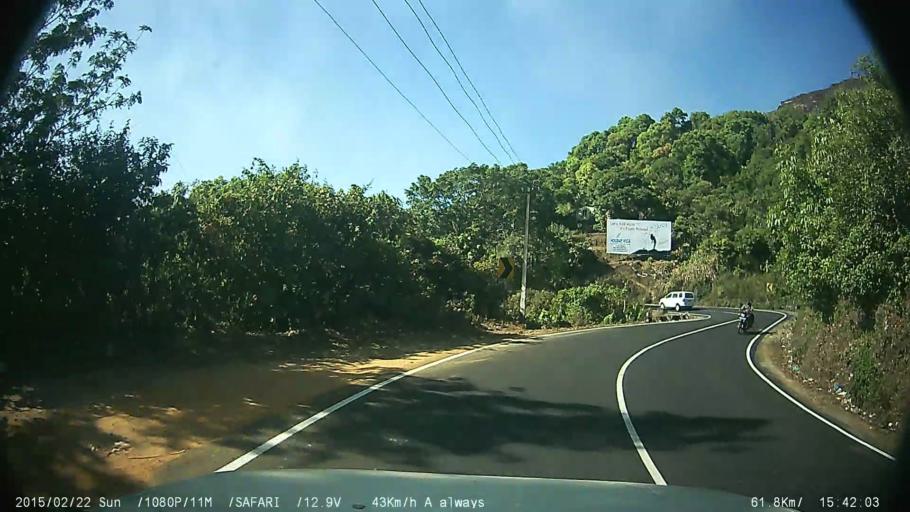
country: IN
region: Kerala
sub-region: Kottayam
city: Erattupetta
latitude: 9.5758
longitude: 76.9736
